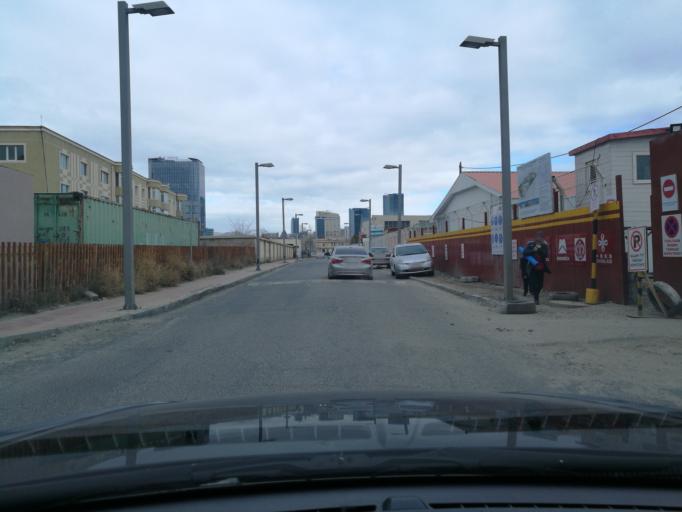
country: MN
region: Ulaanbaatar
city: Ulaanbaatar
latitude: 47.9021
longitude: 106.9207
